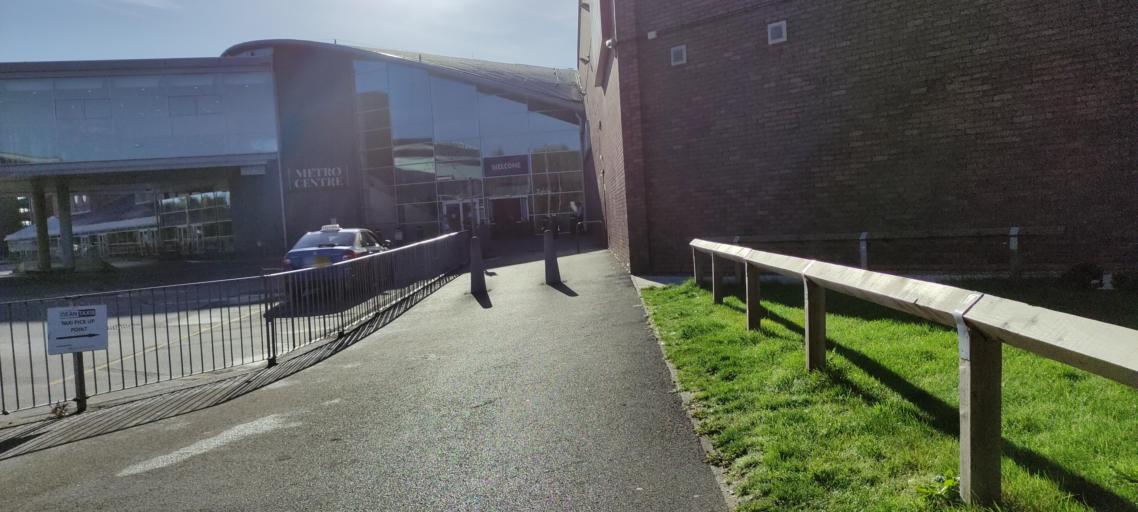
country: GB
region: England
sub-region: Newcastle upon Tyne
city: Benwell
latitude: 54.9584
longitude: -1.6668
